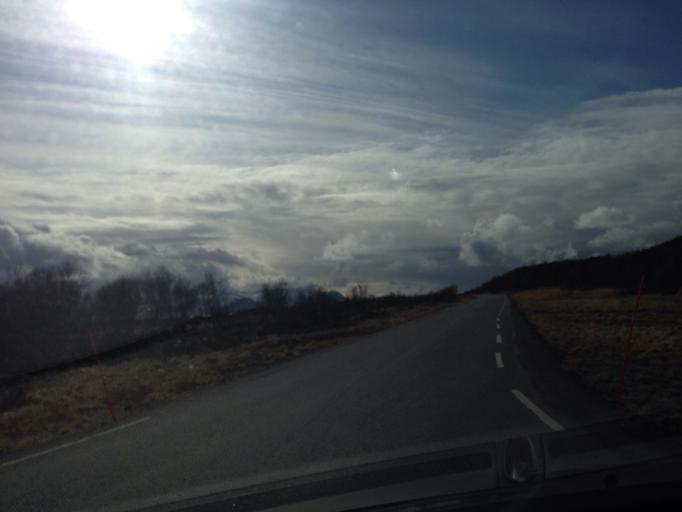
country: NO
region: Nordland
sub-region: Vagan
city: Kabelvag
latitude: 68.3844
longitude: 14.4611
